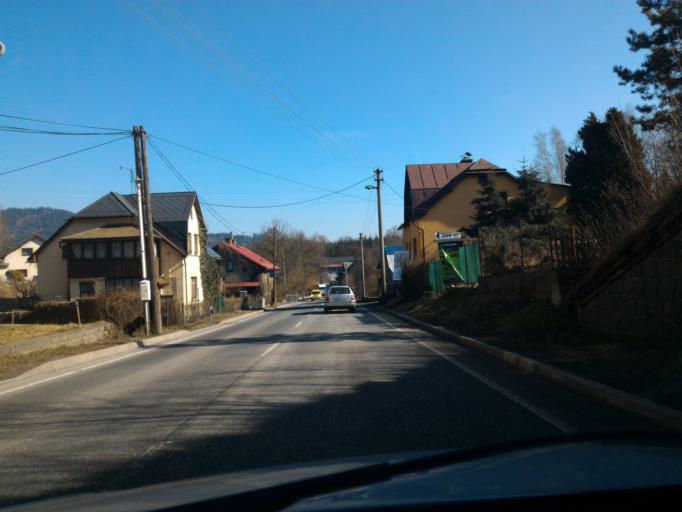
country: CZ
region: Liberecky
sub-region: Okres Jablonec nad Nisou
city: Smrzovka
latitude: 50.7306
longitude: 15.2664
